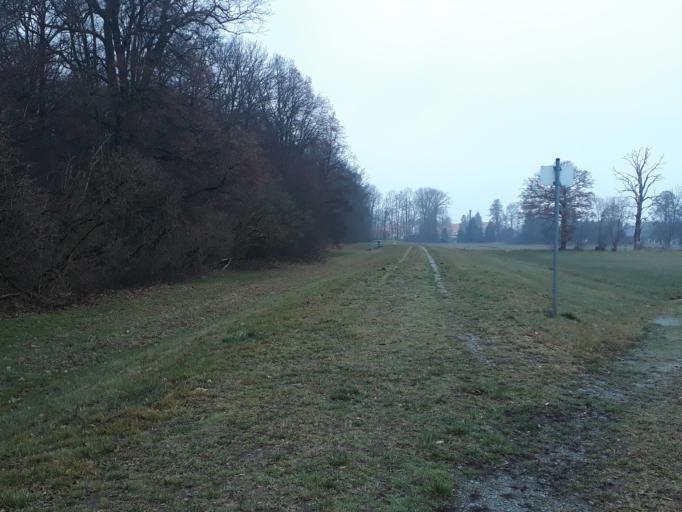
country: DE
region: Saxony
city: Guttau
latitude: 51.2547
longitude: 14.5660
